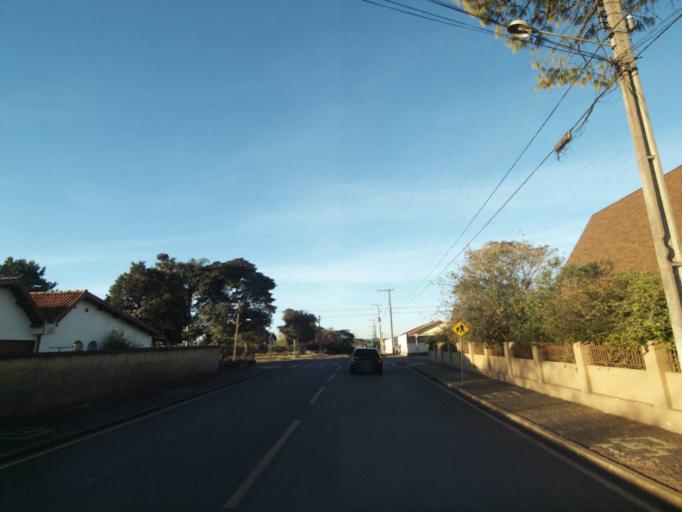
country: BR
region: Parana
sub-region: Tibagi
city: Tibagi
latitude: -24.5106
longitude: -50.4134
